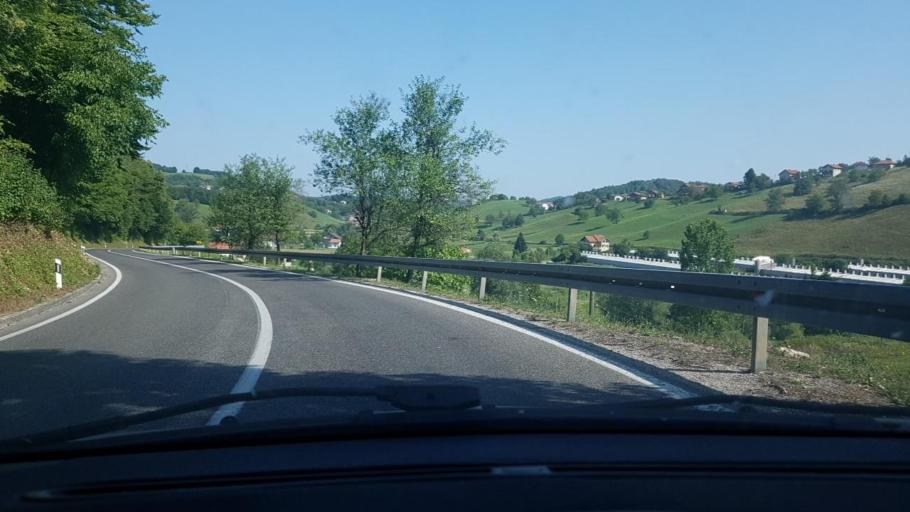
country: BA
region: Federation of Bosnia and Herzegovina
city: Pecigrad
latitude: 45.0641
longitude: 15.8921
